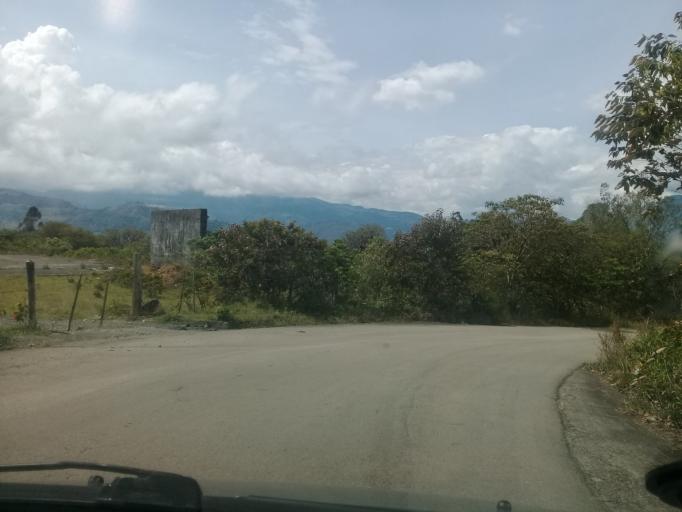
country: CO
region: Cundinamarca
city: Gachala
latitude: 4.6986
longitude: -73.4870
